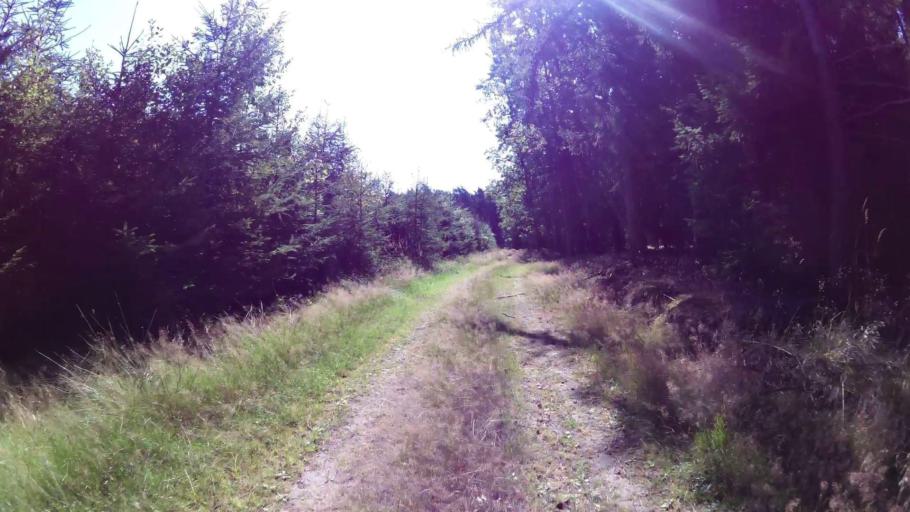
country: PL
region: West Pomeranian Voivodeship
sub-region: Powiat drawski
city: Czaplinek
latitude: 53.4508
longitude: 16.2222
